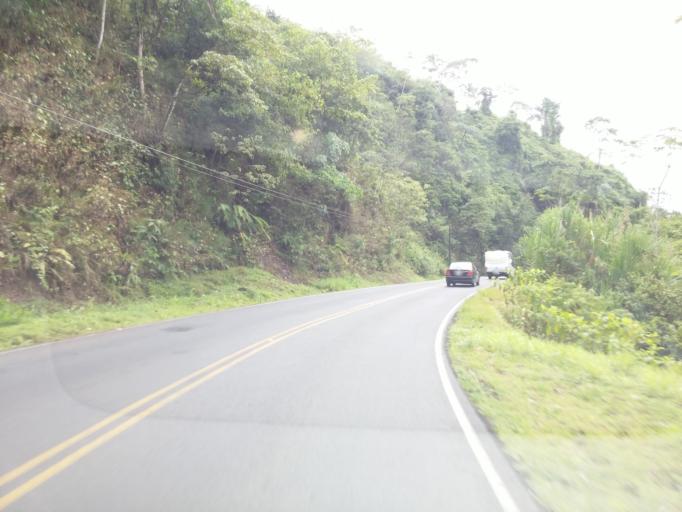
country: CR
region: Alajuela
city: San Ramon
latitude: 10.2175
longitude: -84.5451
